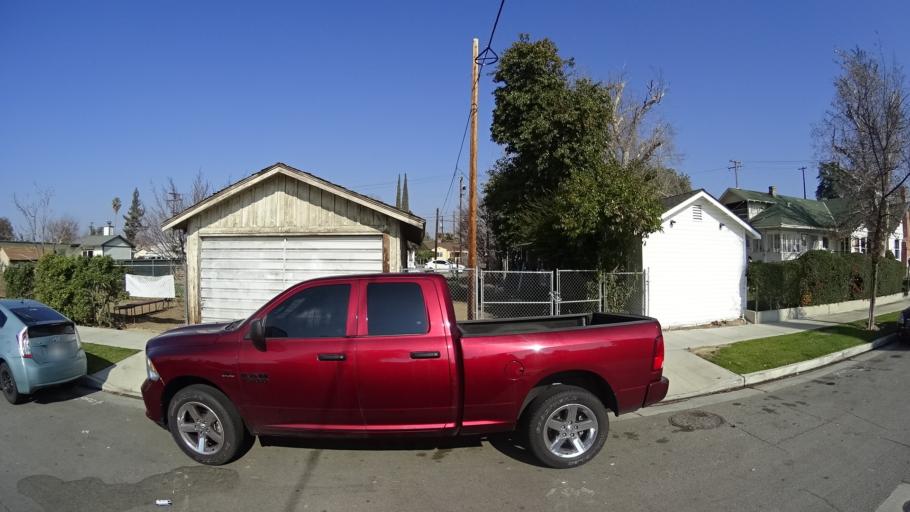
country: US
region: California
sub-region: Kern County
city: Bakersfield
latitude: 35.3896
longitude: -118.9890
